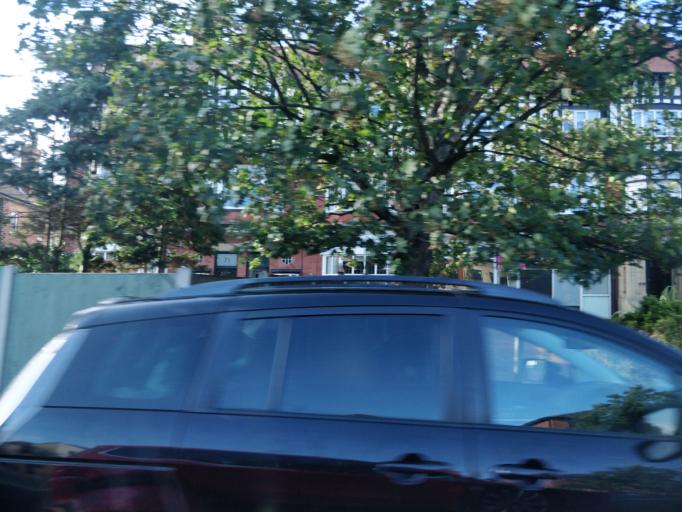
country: GB
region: England
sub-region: Sefton
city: Southport
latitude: 53.6540
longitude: -2.9901
